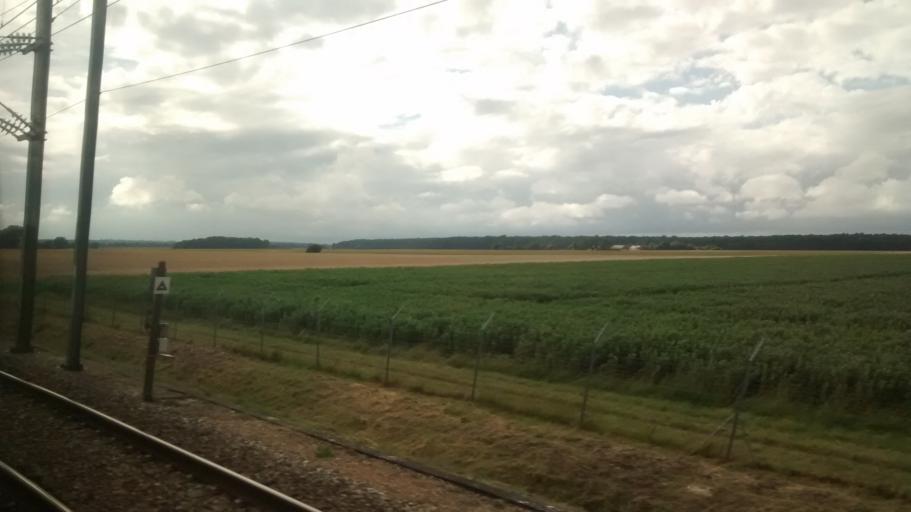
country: FR
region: Centre
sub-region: Departement du Loir-et-Cher
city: Droue
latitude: 48.0791
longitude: 1.0890
